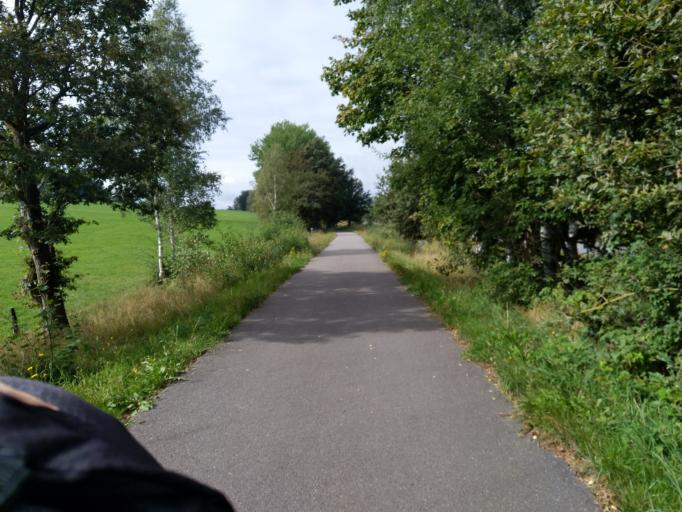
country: BE
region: Wallonia
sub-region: Province de Liege
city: Malmedy
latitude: 50.4127
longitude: 5.9806
